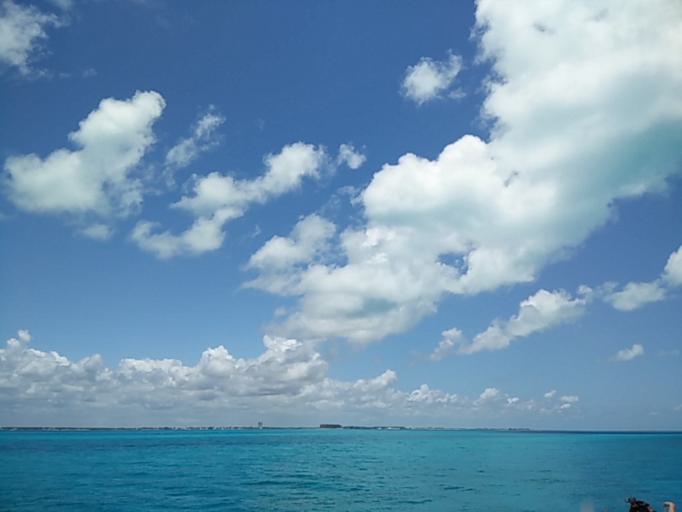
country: MX
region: Quintana Roo
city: Isla Mujeres
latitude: 21.2092
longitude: -86.7591
